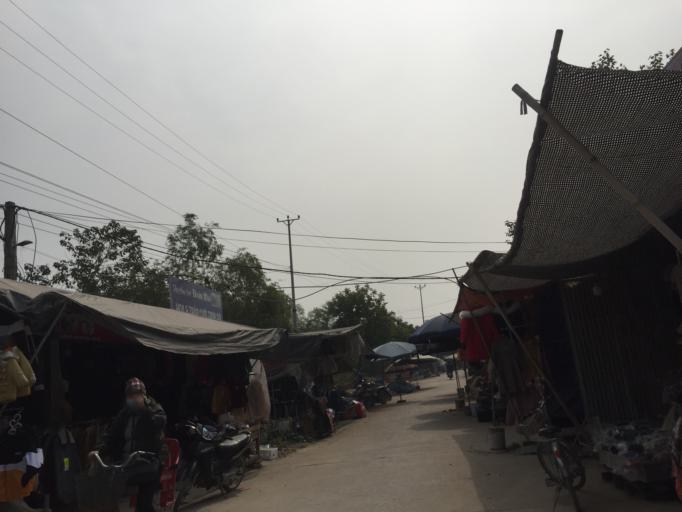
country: VN
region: Hung Yen
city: Van Giang
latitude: 20.9634
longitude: 105.9184
